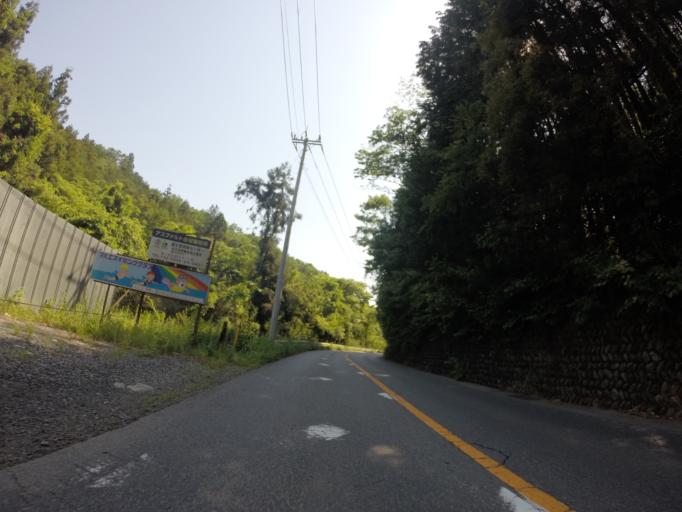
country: JP
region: Shizuoka
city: Fujinomiya
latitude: 35.2037
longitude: 138.6053
